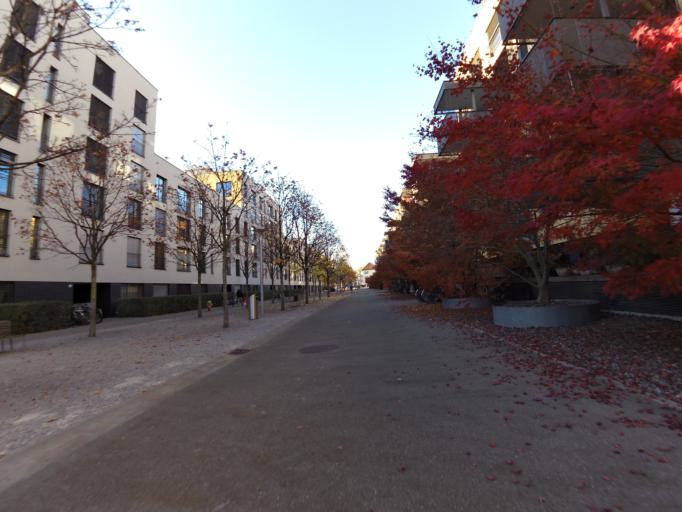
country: CH
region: Zurich
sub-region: Bezirk Zuerich
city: Zuerich (Kreis 3) / Alt-Wiedikon
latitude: 47.3652
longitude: 8.5153
